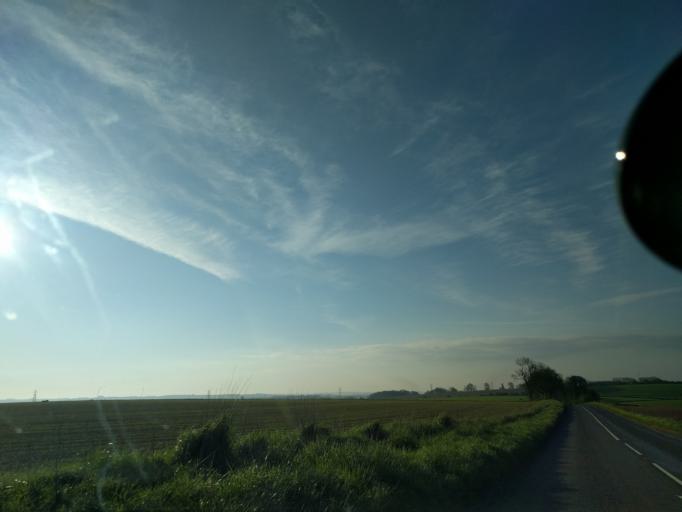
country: GB
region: England
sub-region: Wiltshire
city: Woodford
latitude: 51.1126
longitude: -1.8484
